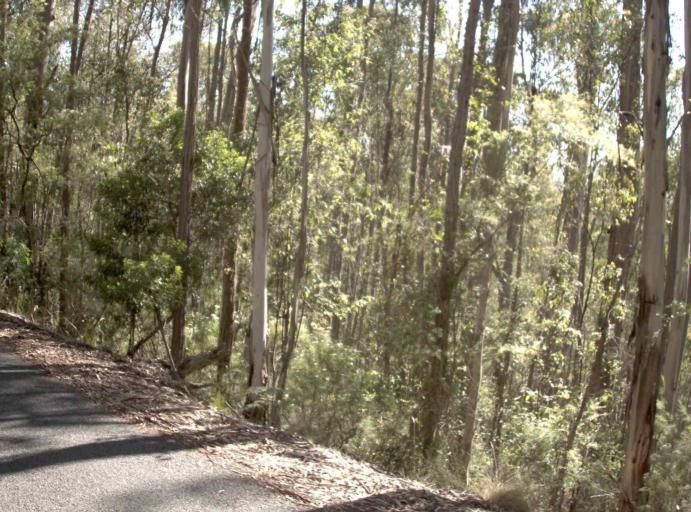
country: AU
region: New South Wales
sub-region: Bombala
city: Bombala
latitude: -37.3852
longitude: 148.6262
